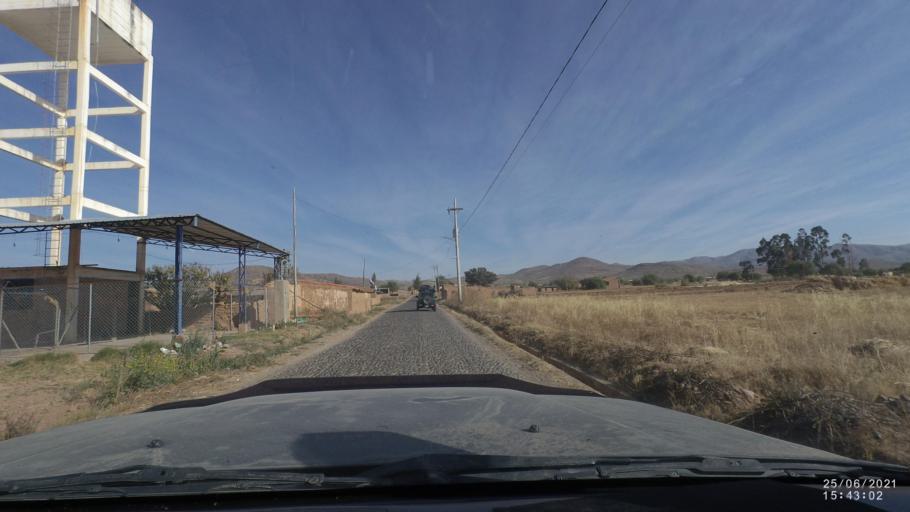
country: BO
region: Cochabamba
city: Cliza
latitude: -17.6443
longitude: -65.9119
